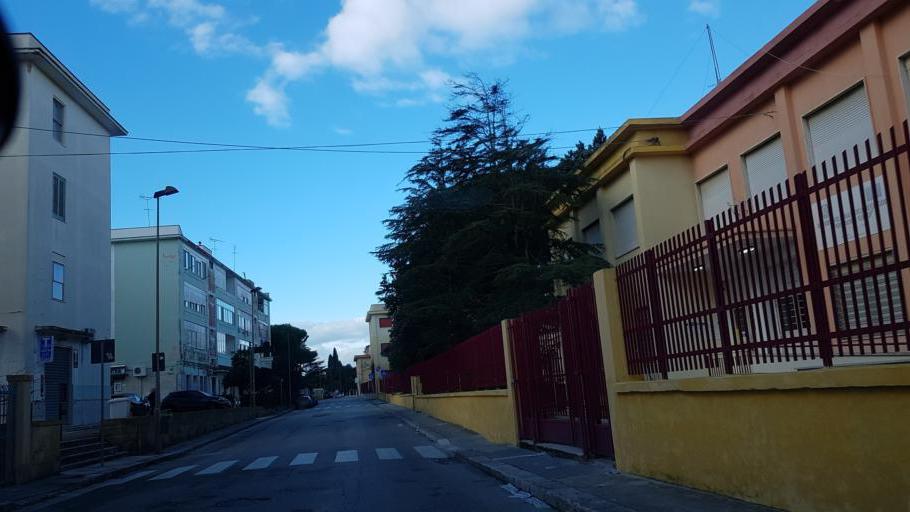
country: IT
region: Apulia
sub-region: Provincia di Brindisi
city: Brindisi
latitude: 40.6452
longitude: 17.9408
